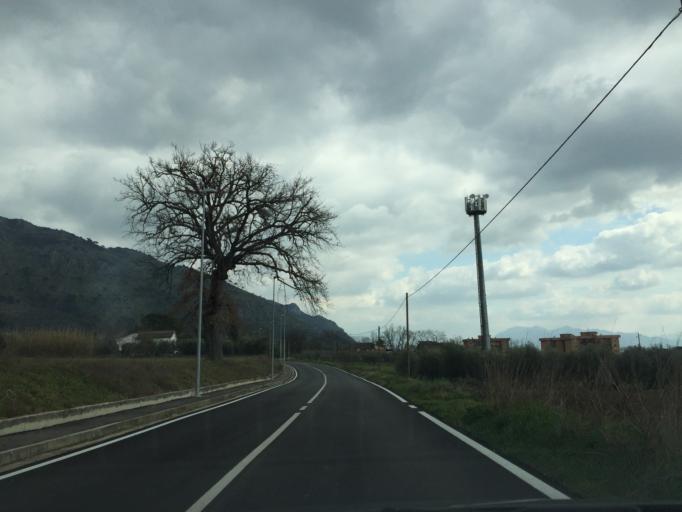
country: IT
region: Latium
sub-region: Provincia di Frosinone
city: Piedimonte San Germano
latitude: 41.4970
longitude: 13.7653
